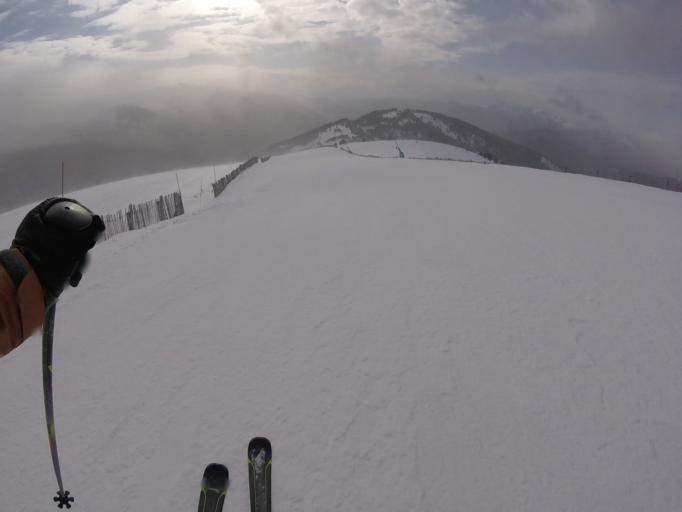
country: AD
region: Canillo
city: Canillo
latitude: 42.5492
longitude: 1.6230
